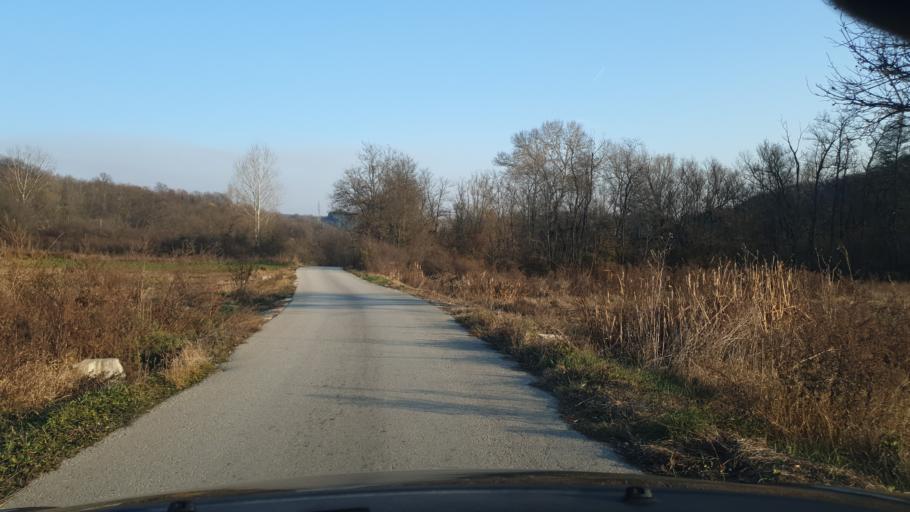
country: RS
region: Central Serbia
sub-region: Zajecarski Okrug
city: Zajecar
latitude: 44.0287
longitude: 22.3345
